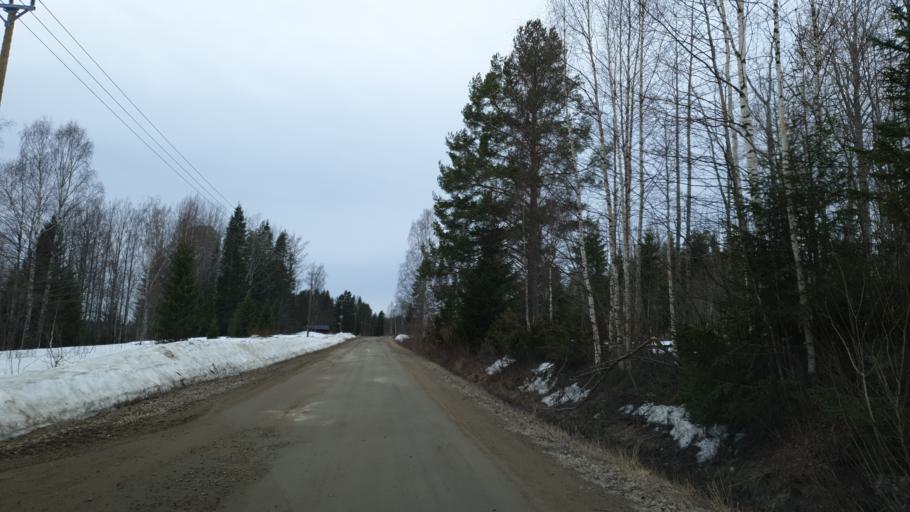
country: SE
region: Vaesterbotten
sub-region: Robertsfors Kommun
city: Robertsfors
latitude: 64.3909
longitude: 20.9728
